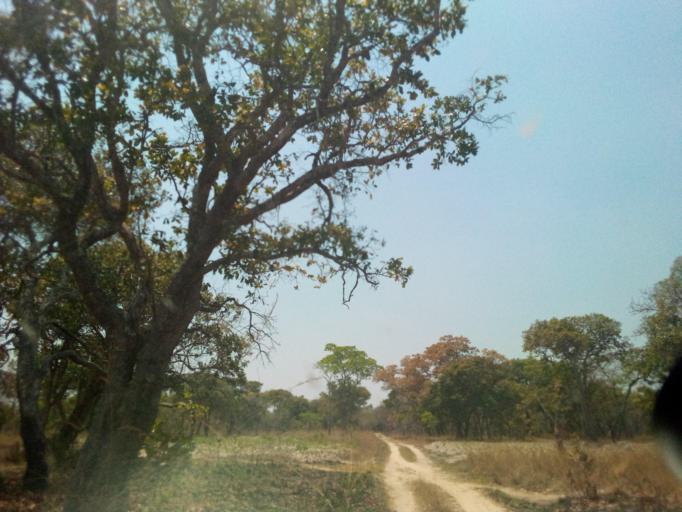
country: ZM
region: Copperbelt
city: Kataba
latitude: -12.2389
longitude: 30.4043
